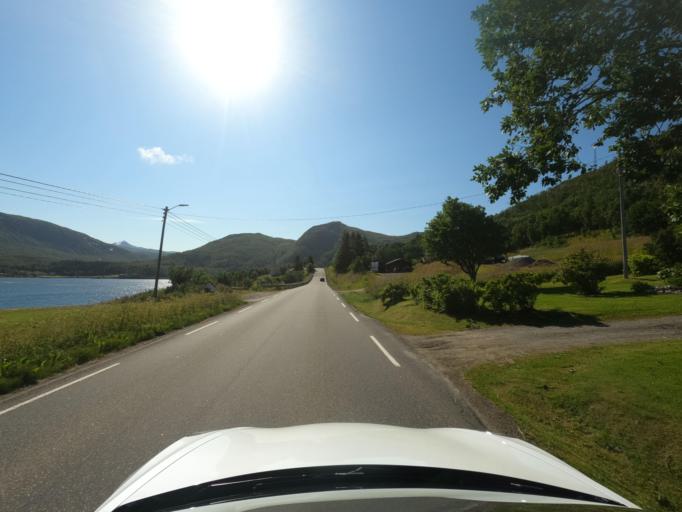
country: NO
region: Nordland
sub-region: Lodingen
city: Lodingen
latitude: 68.5686
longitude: 15.7983
